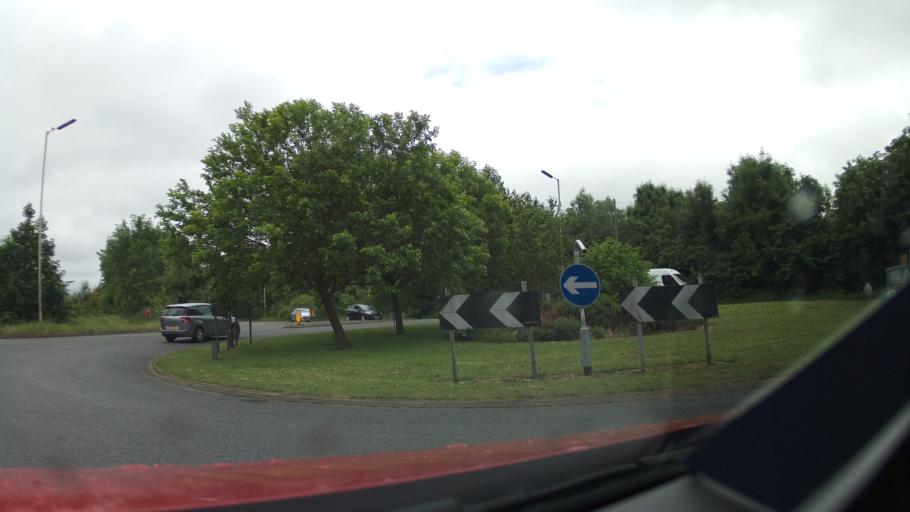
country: GB
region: England
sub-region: Staffordshire
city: Burton upon Trent
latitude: 52.8533
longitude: -1.6800
